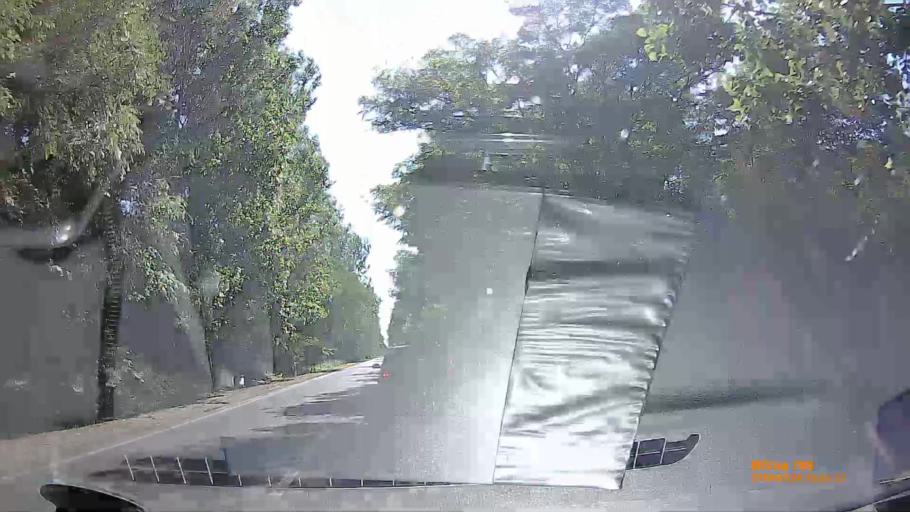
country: HU
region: Szabolcs-Szatmar-Bereg
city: Vaja
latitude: 48.0128
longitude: 22.1334
